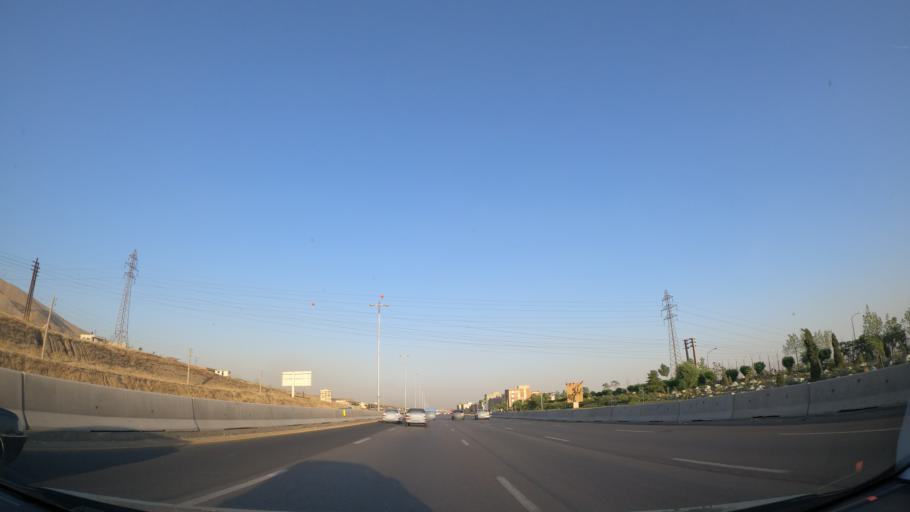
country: IR
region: Tehran
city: Shahr-e Qods
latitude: 35.7608
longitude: 51.0637
